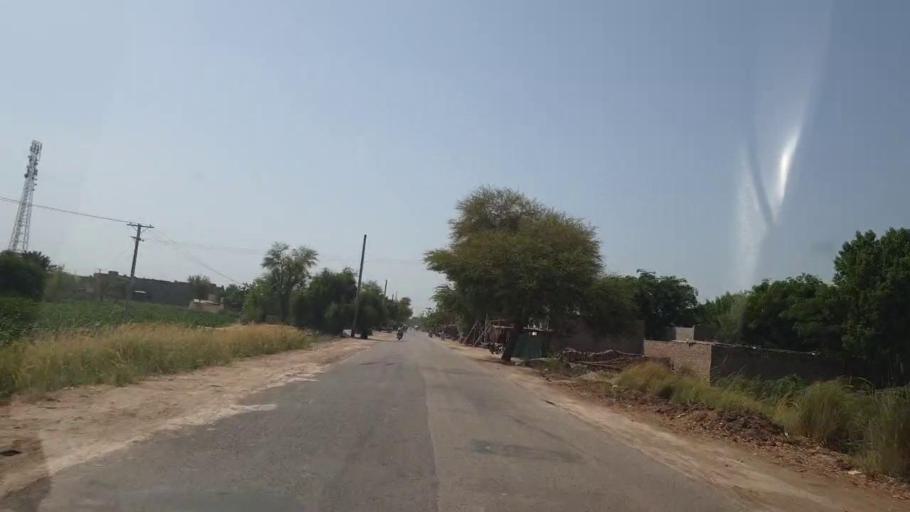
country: PK
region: Sindh
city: Setharja Old
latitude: 27.1286
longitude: 68.5366
